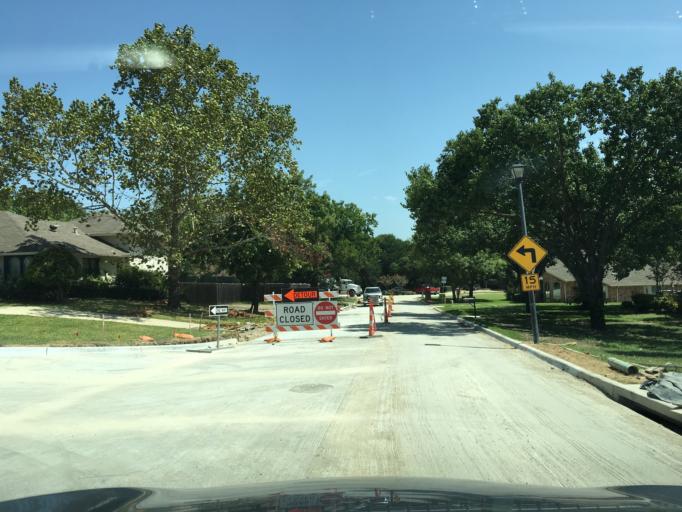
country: US
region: Texas
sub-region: Dallas County
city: Rowlett
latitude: 32.8745
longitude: -96.5999
